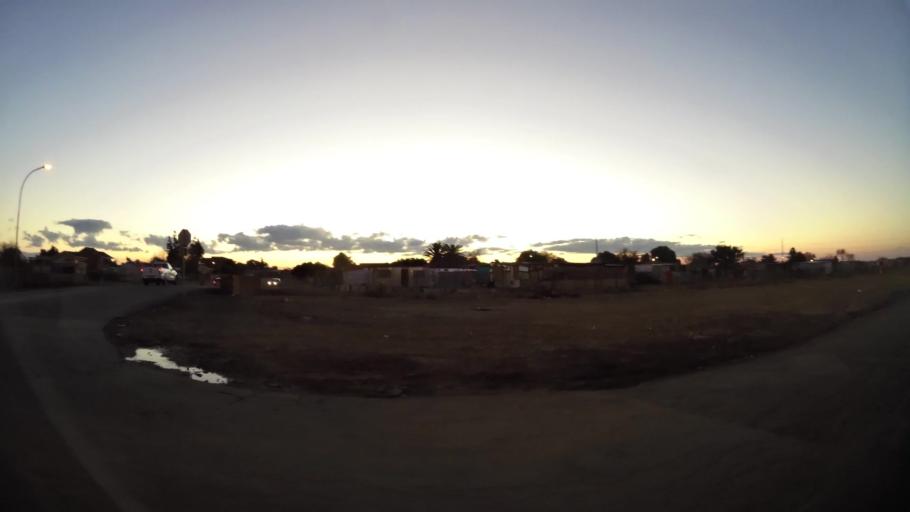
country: ZA
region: Northern Cape
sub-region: Frances Baard District Municipality
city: Kimberley
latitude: -28.7155
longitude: 24.7635
